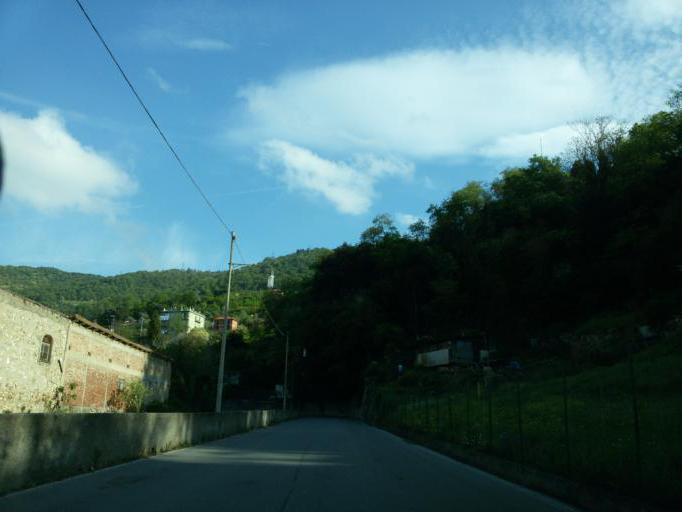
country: IT
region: Liguria
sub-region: Provincia di Genova
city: Piccarello
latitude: 44.4618
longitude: 8.9781
